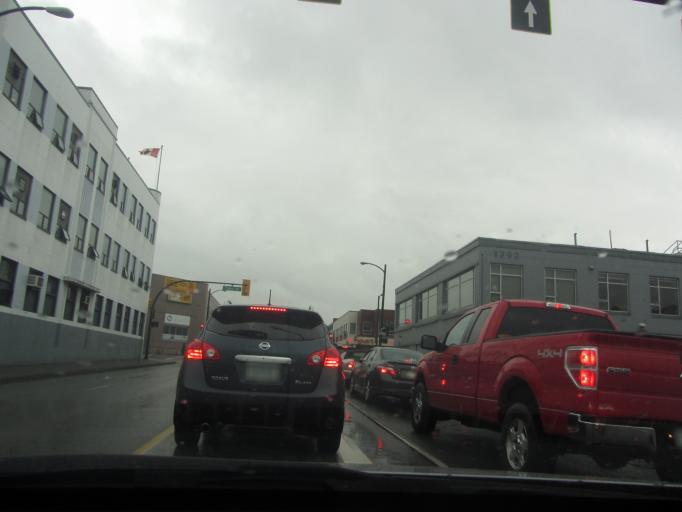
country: CA
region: British Columbia
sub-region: Fraser Valley Regional District
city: North Vancouver
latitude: 49.2767
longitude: -123.0780
